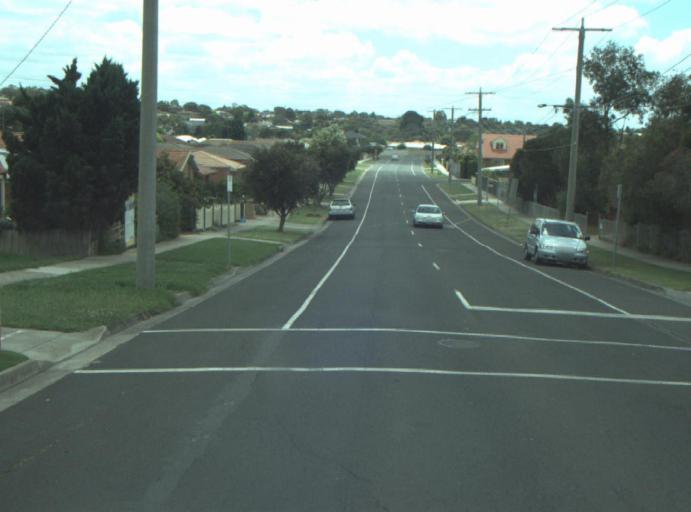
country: AU
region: Victoria
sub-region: Greater Geelong
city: Wandana Heights
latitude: -38.2001
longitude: 144.3269
